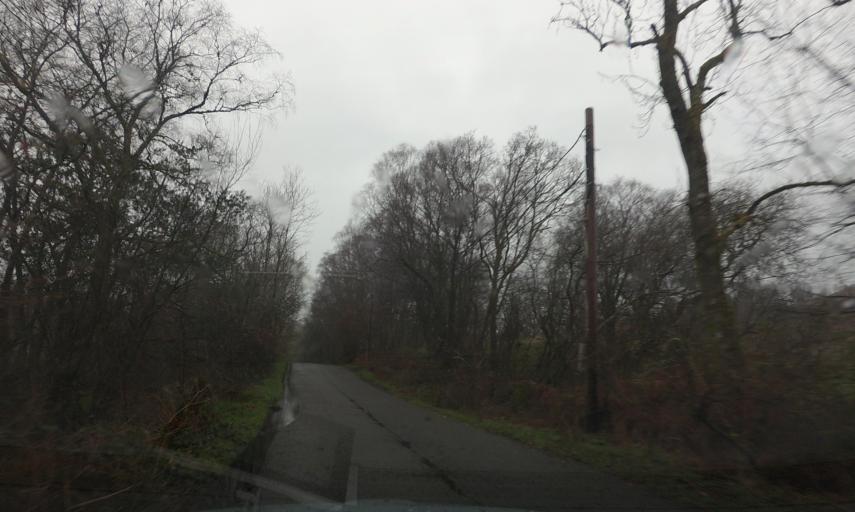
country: GB
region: Scotland
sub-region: West Dunbartonshire
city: Balloch
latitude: 56.1416
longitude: -4.6220
